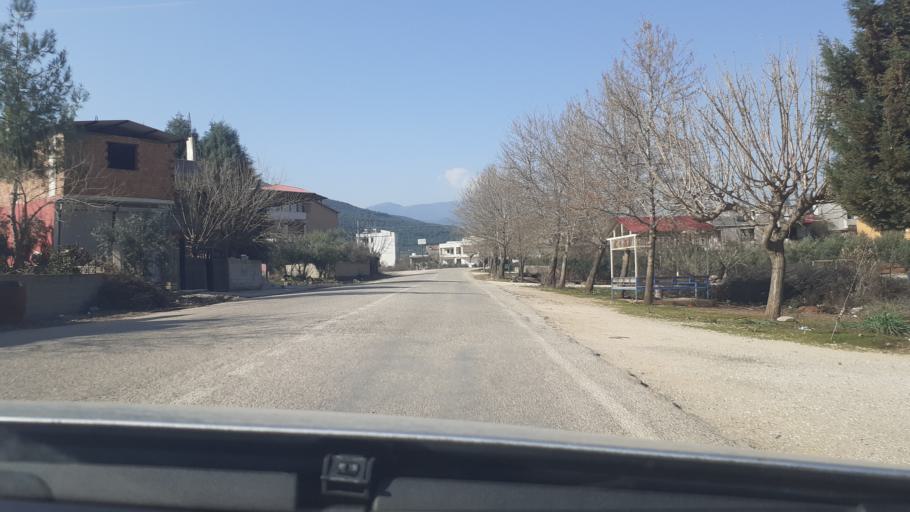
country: TR
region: Hatay
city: Aktepe
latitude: 36.7099
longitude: 36.4865
